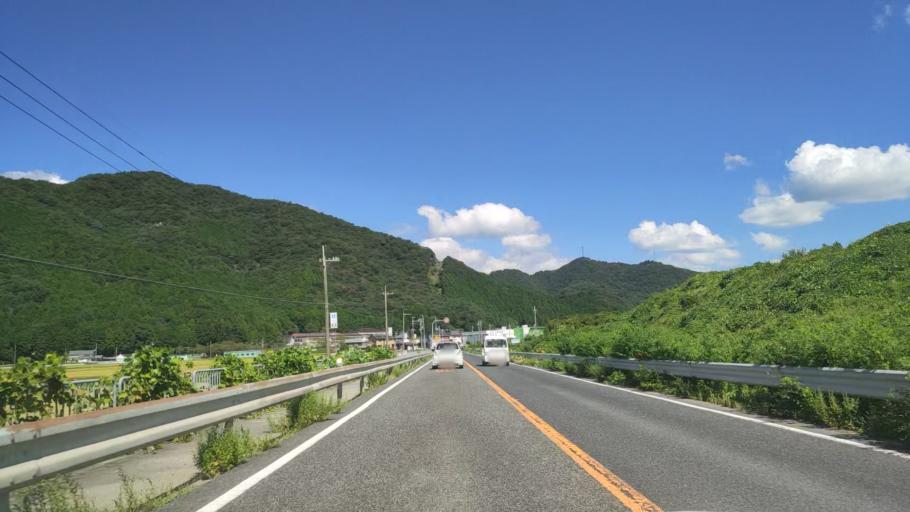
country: JP
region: Hyogo
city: Nishiwaki
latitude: 35.0505
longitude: 134.9886
